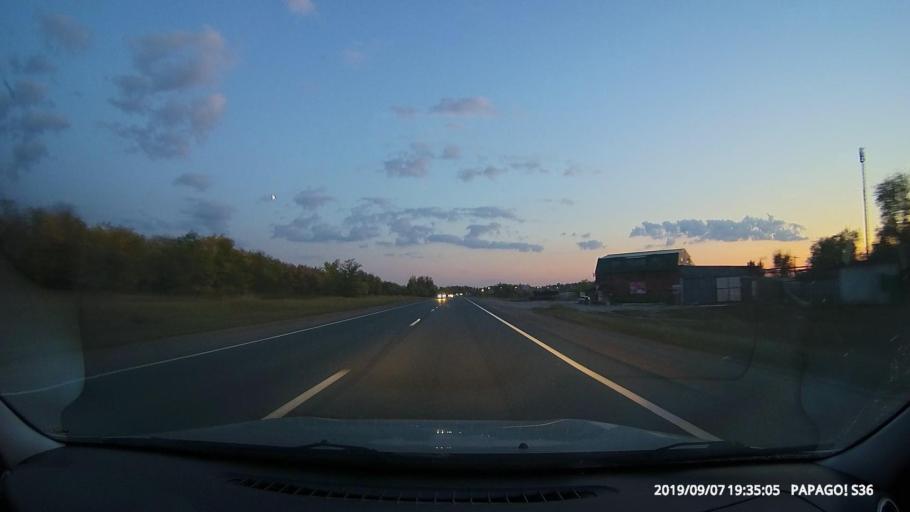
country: RU
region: Samara
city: Chapayevsk
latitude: 52.9972
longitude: 49.7663
